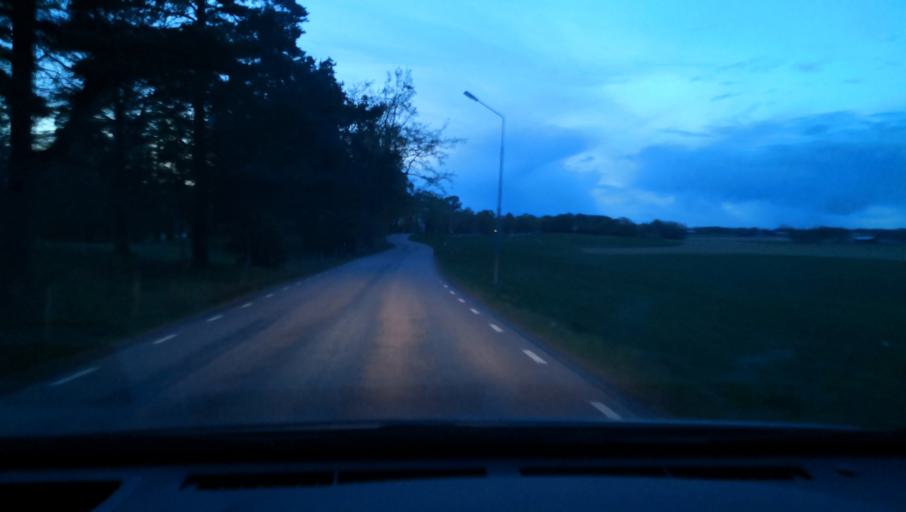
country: SE
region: OErebro
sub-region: Askersunds Kommun
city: Asbro
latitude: 59.0954
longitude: 15.0078
